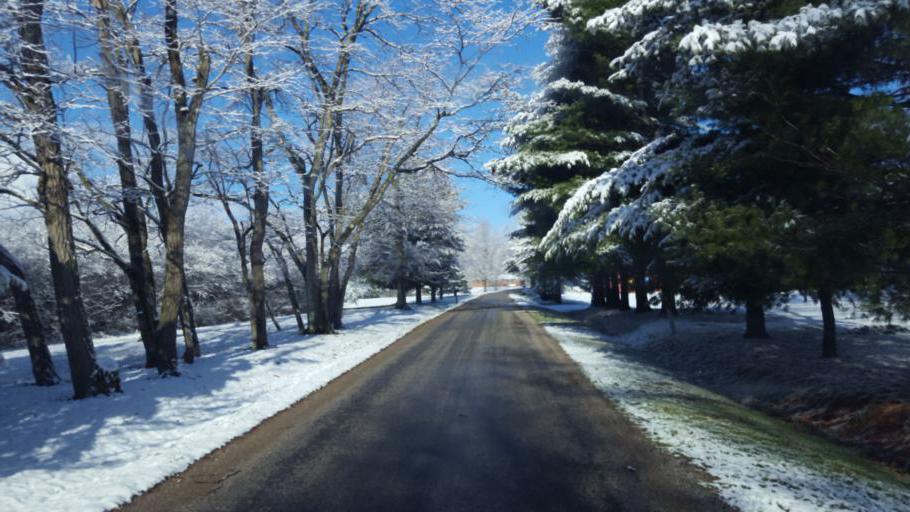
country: US
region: Ohio
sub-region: Knox County
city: Fredericktown
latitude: 40.4886
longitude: -82.6426
